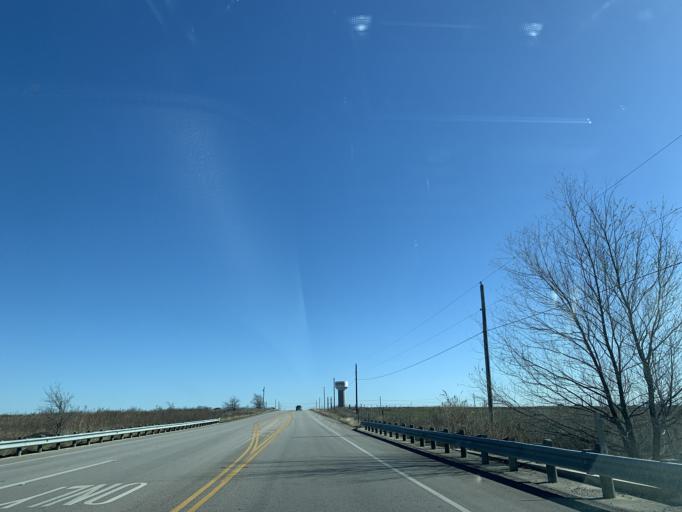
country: US
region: Texas
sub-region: Williamson County
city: Hutto
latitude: 30.5585
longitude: -97.5697
